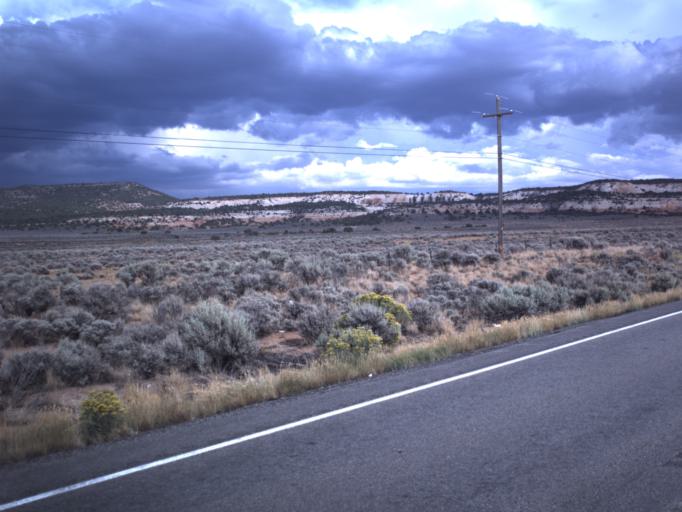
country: US
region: Utah
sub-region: Grand County
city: Moab
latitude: 38.2925
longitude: -109.3823
